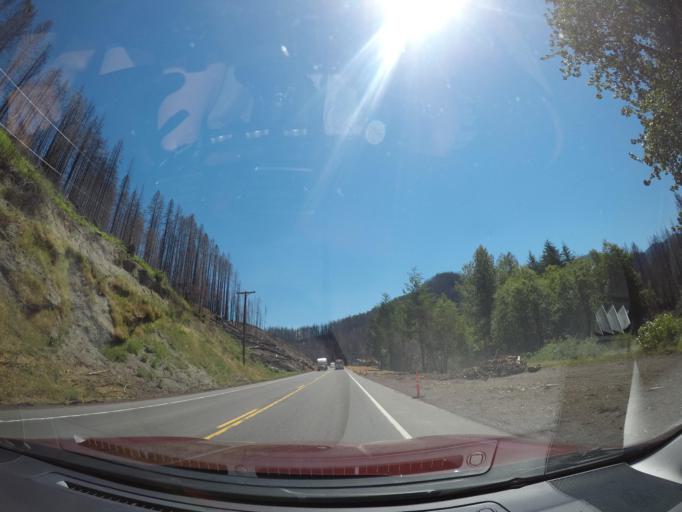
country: US
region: Oregon
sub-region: Linn County
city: Mill City
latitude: 44.6877
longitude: -122.0360
